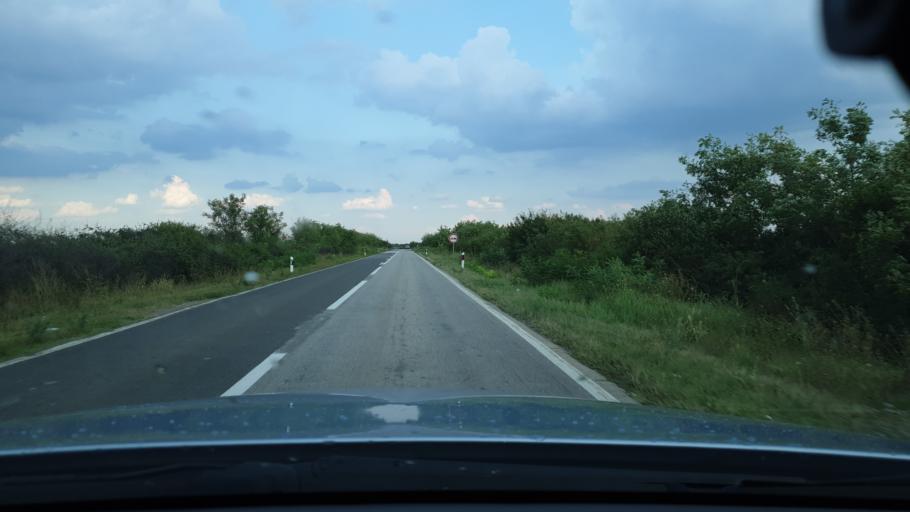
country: RS
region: Autonomna Pokrajina Vojvodina
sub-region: Srednjebanatski Okrug
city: Secanj
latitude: 45.3488
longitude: 20.7953
